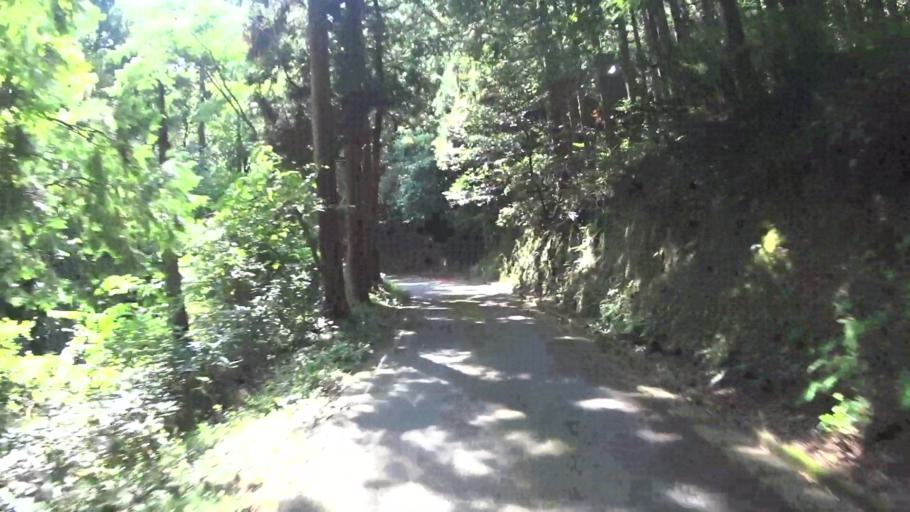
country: JP
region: Kyoto
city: Miyazu
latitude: 35.6581
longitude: 135.1220
